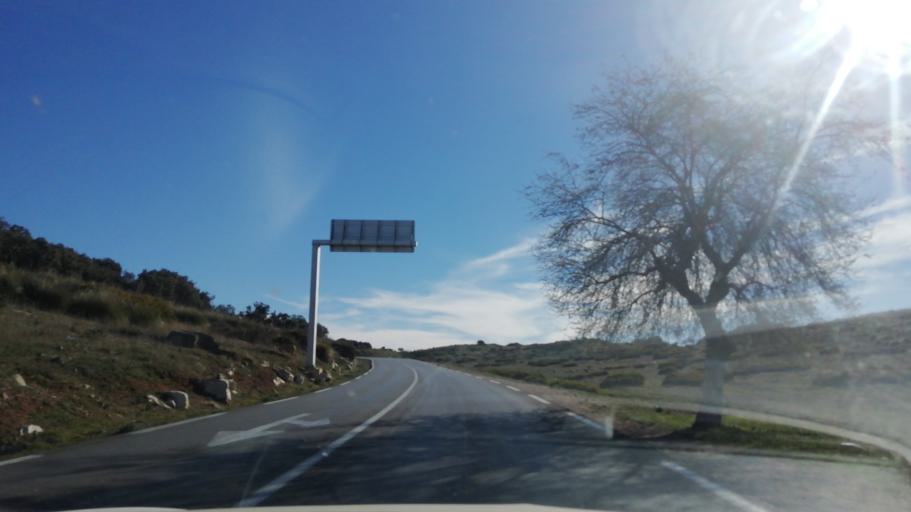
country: DZ
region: Tlemcen
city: Mansoura
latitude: 34.8300
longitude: -1.3709
